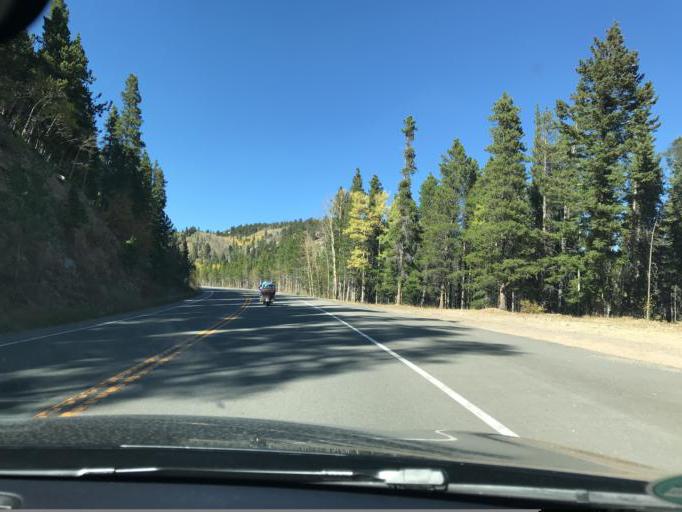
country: US
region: Colorado
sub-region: Boulder County
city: Nederland
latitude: 40.0655
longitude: -105.5152
